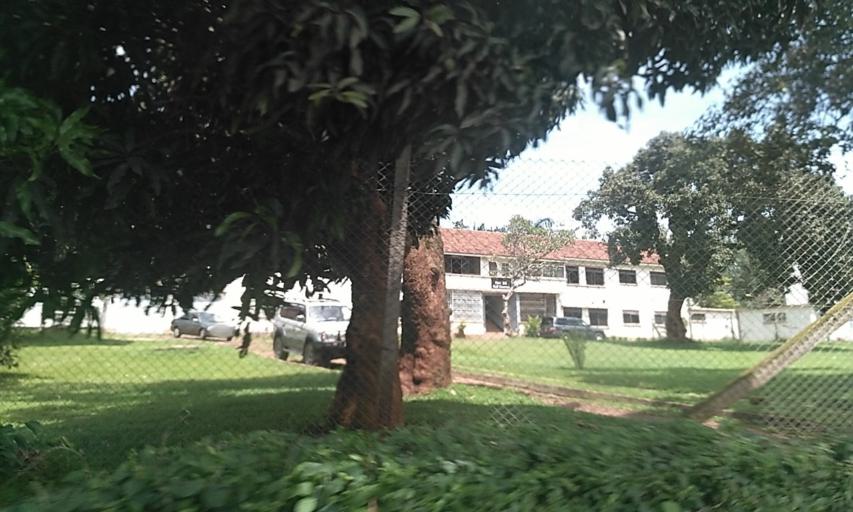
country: UG
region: Central Region
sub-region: Kampala District
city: Kampala
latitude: 0.3215
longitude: 32.5946
